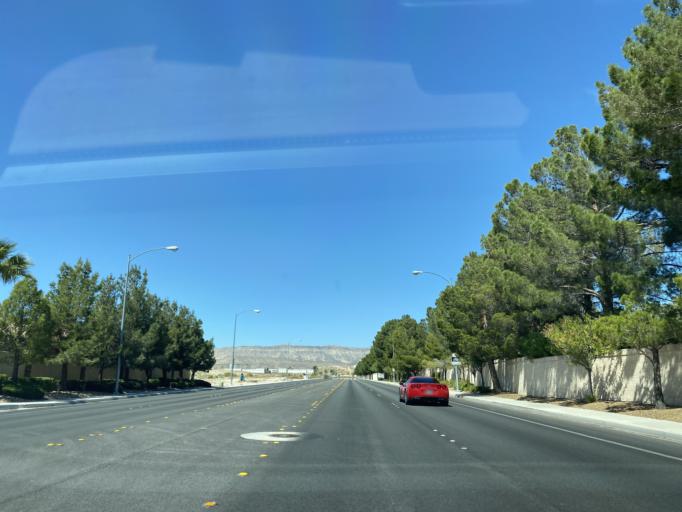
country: US
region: Nevada
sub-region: Clark County
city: Spring Valley
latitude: 36.0925
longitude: -115.2704
